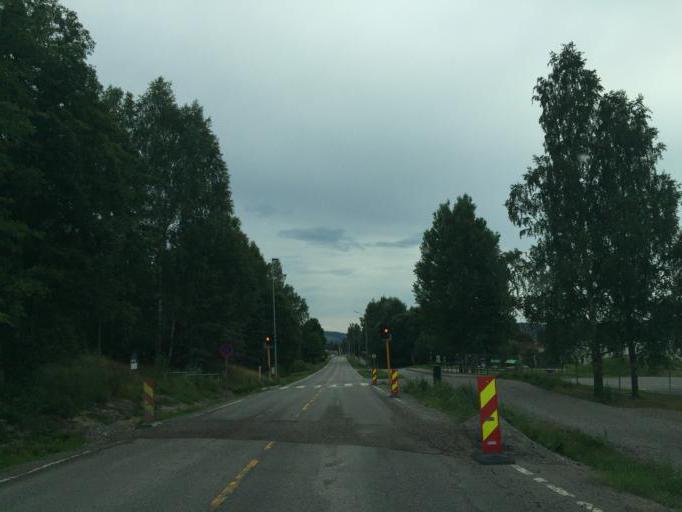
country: NO
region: Hedmark
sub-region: Kongsvinger
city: Kongsvinger
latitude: 60.1994
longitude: 11.9921
